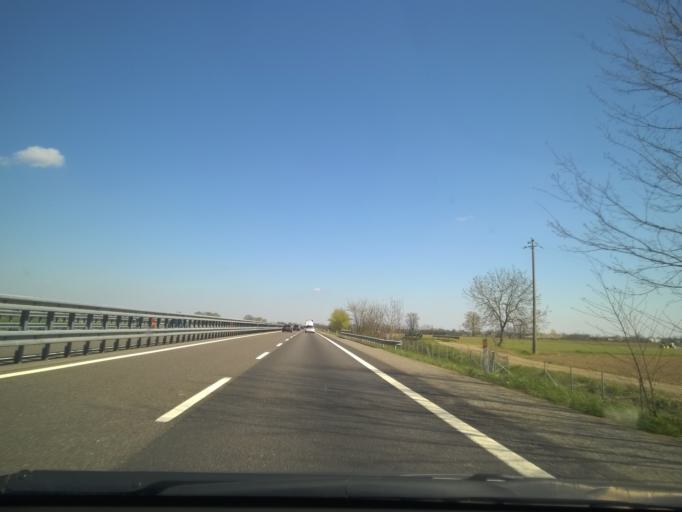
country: IT
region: Emilia-Romagna
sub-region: Provincia di Piacenza
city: Rottofreno
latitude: 45.0647
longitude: 9.5706
